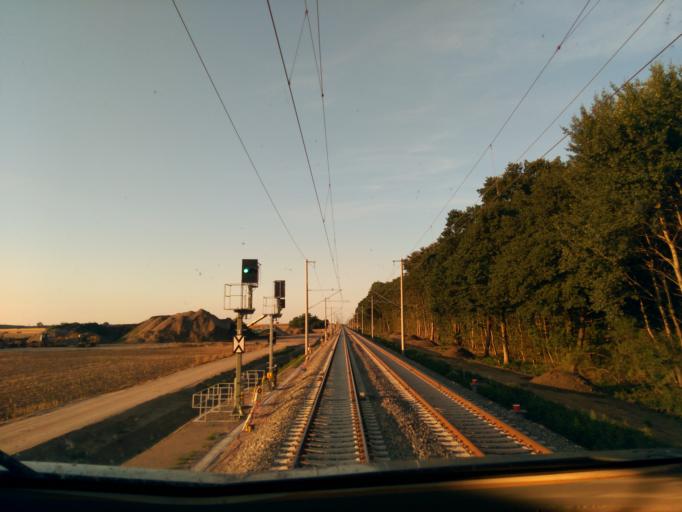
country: DE
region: Mecklenburg-Vorpommern
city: Lubstorf
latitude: 53.7435
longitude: 11.4227
